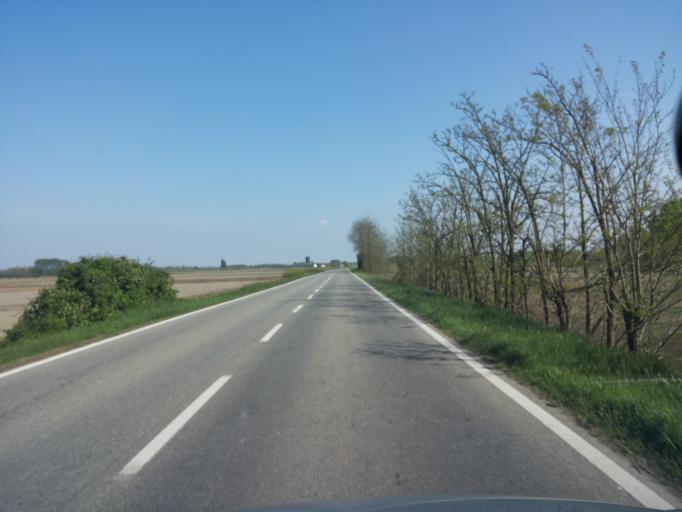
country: IT
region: Piedmont
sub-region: Provincia di Vercelli
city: Caresana
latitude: 45.2145
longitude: 8.5098
